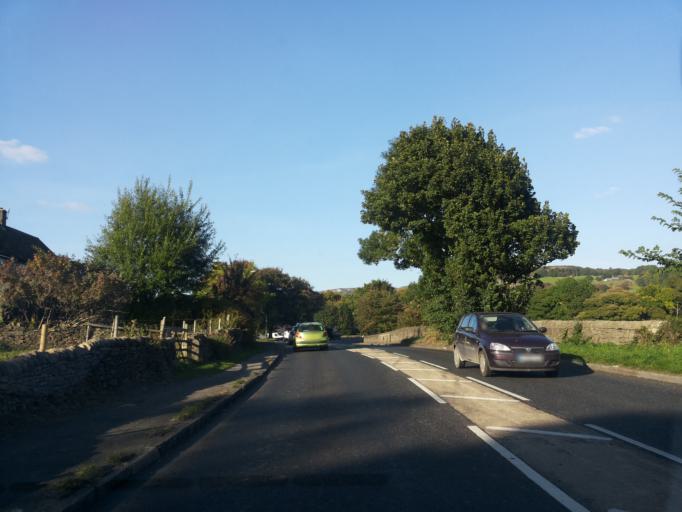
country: GB
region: England
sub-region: Derbyshire
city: Bakewell
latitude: 53.2442
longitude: -1.6249
